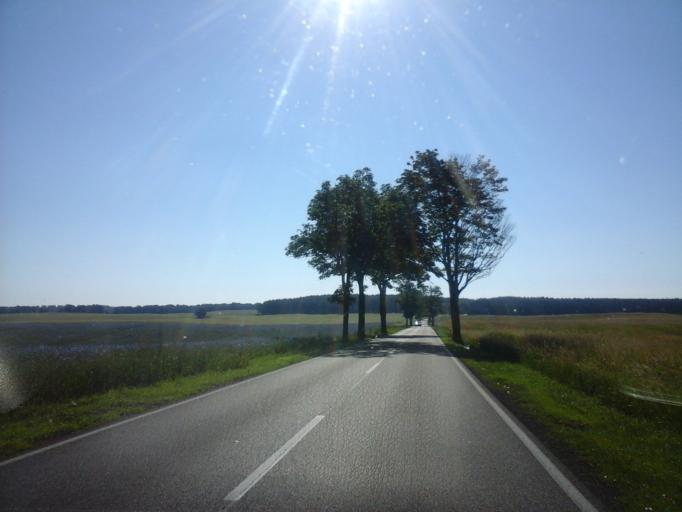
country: PL
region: West Pomeranian Voivodeship
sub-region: Powiat drawski
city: Drawsko Pomorskie
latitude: 53.4974
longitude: 15.6833
